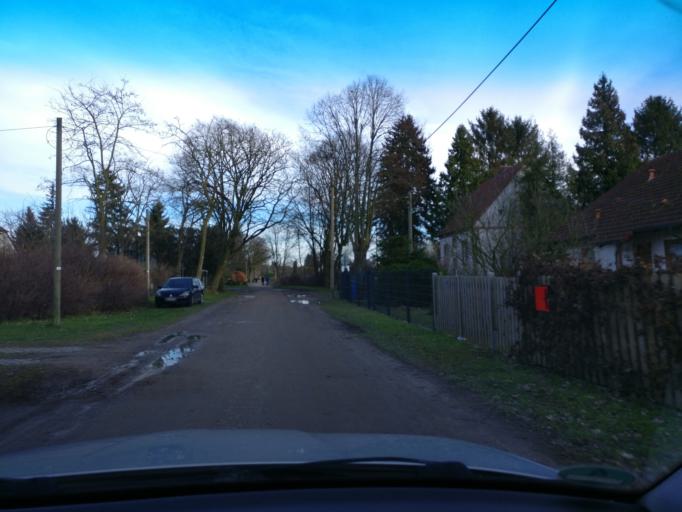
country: DE
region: Brandenburg
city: Bernau bei Berlin
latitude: 52.6655
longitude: 13.5431
